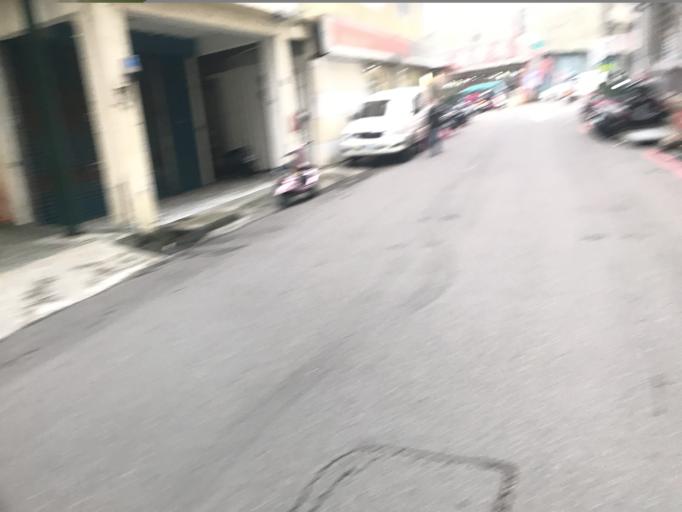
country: TW
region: Taiwan
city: Taoyuan City
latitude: 24.9540
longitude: 121.2370
